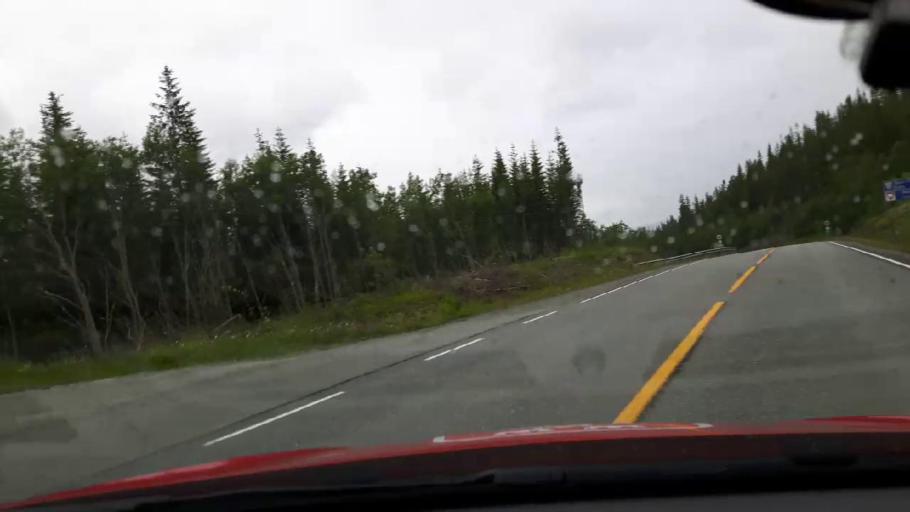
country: NO
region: Nord-Trondelag
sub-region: Meraker
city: Meraker
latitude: 63.3365
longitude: 12.0589
